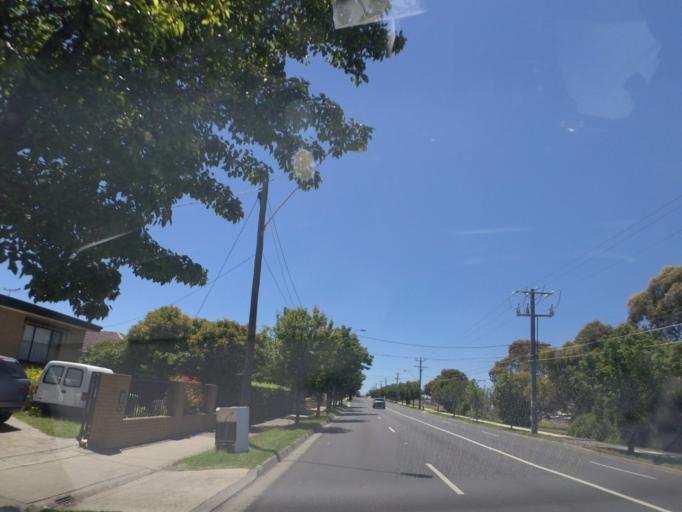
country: AU
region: Victoria
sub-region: Whittlesea
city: Thomastown
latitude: -37.6754
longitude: 145.0147
